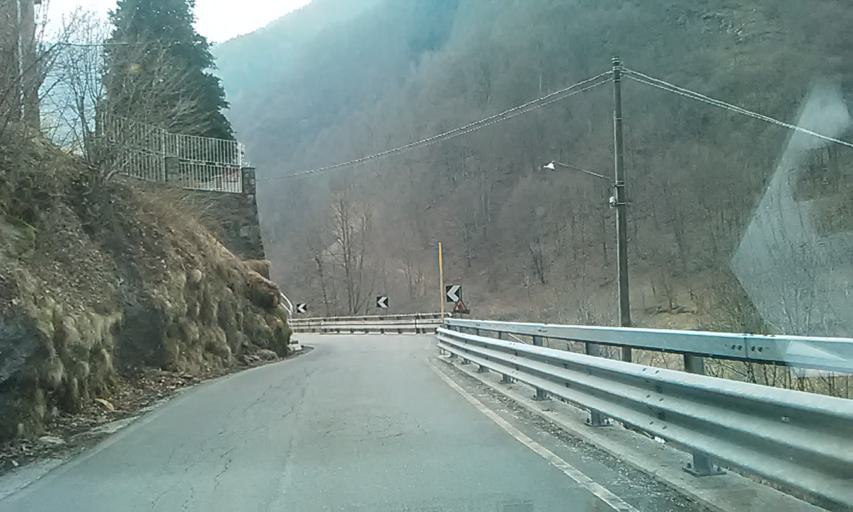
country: IT
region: Piedmont
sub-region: Provincia di Vercelli
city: Fobello
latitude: 45.8974
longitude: 8.1535
